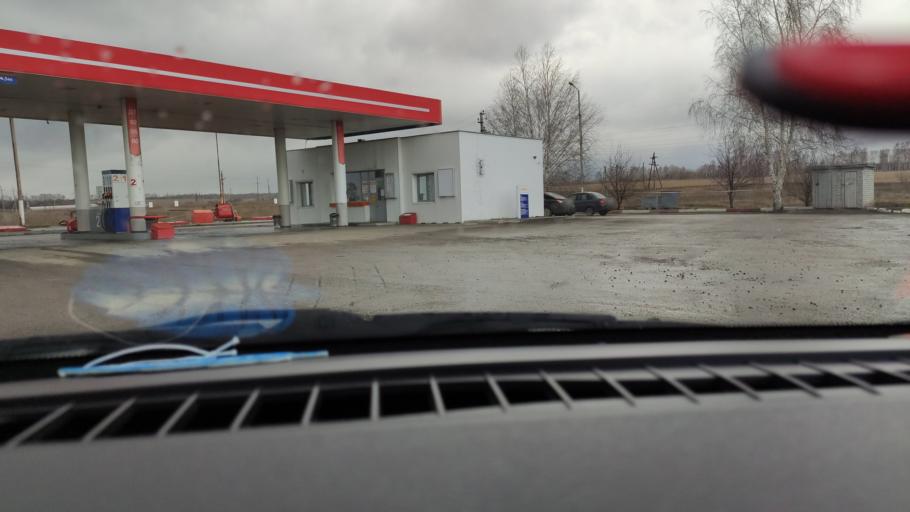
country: RU
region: Samara
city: Koshki
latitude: 54.1629
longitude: 50.4121
